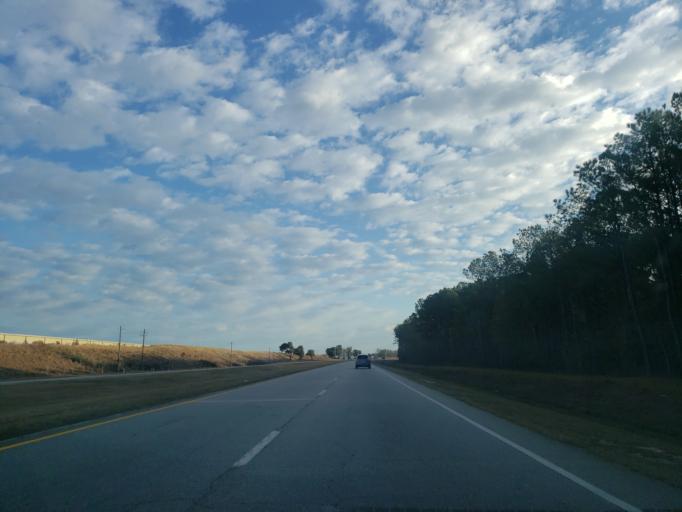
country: US
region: Georgia
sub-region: Chatham County
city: Bloomingdale
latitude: 32.1567
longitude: -81.2734
